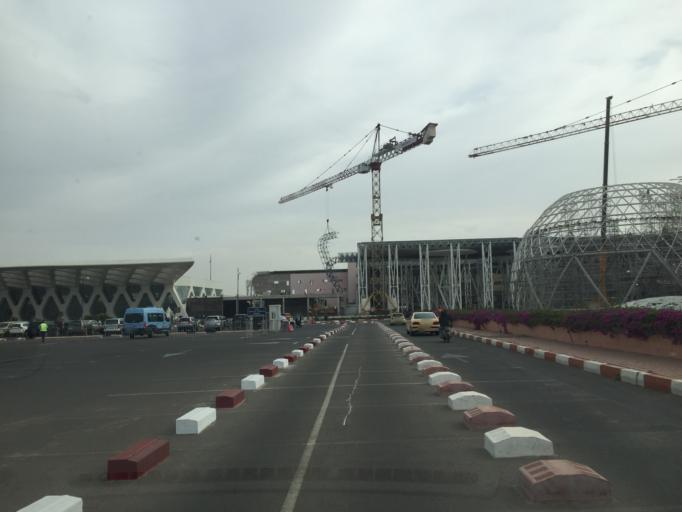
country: MA
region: Marrakech-Tensift-Al Haouz
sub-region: Marrakech
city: Marrakesh
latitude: 31.5999
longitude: -8.0257
